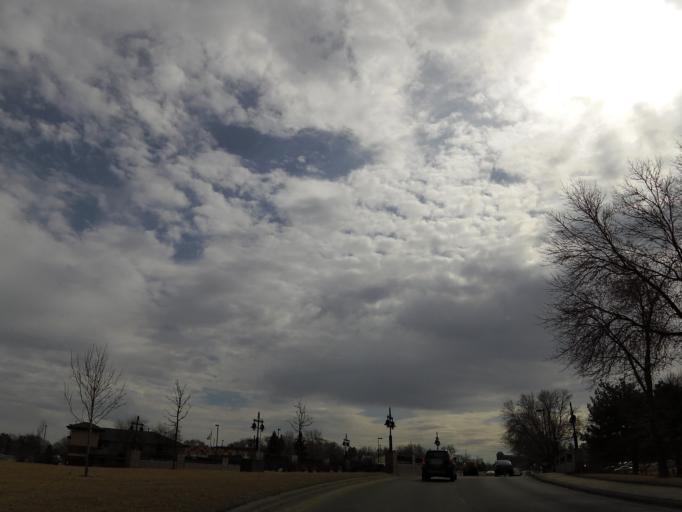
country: US
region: Minnesota
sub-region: Hennepin County
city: Edina
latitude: 44.8715
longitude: -93.3216
